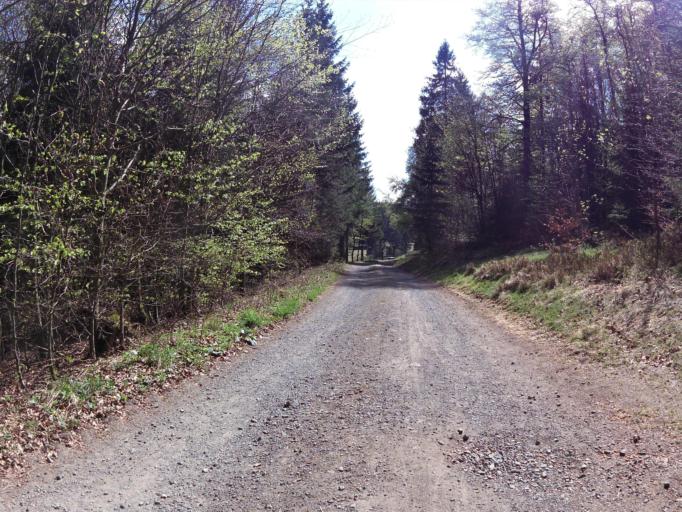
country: DE
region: Thuringia
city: Pappenheim
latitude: 50.7853
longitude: 10.5375
